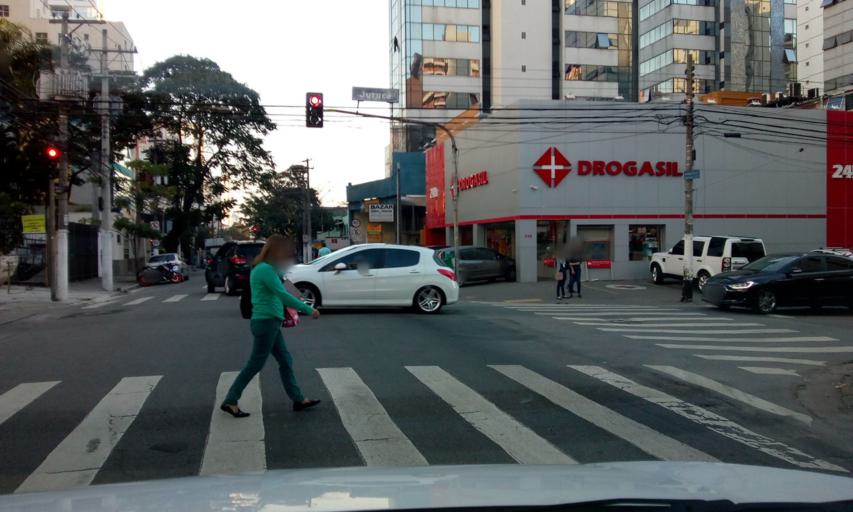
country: BR
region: Sao Paulo
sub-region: Sao Paulo
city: Sao Paulo
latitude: -23.6084
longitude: -46.6622
